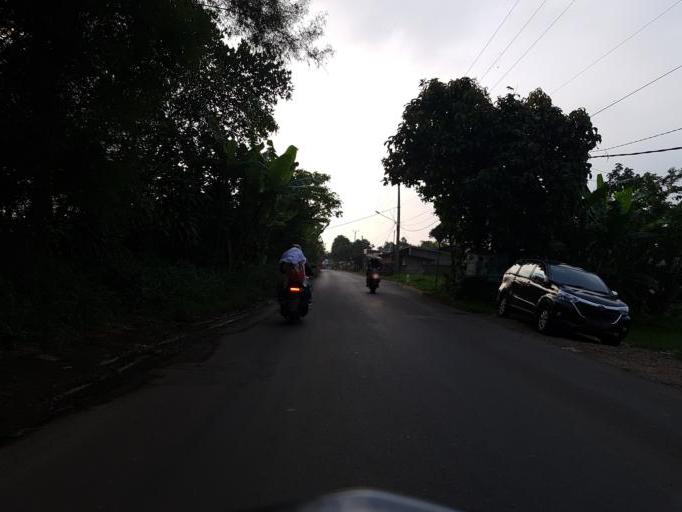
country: ID
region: West Java
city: Parung
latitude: -6.4700
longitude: 106.7177
